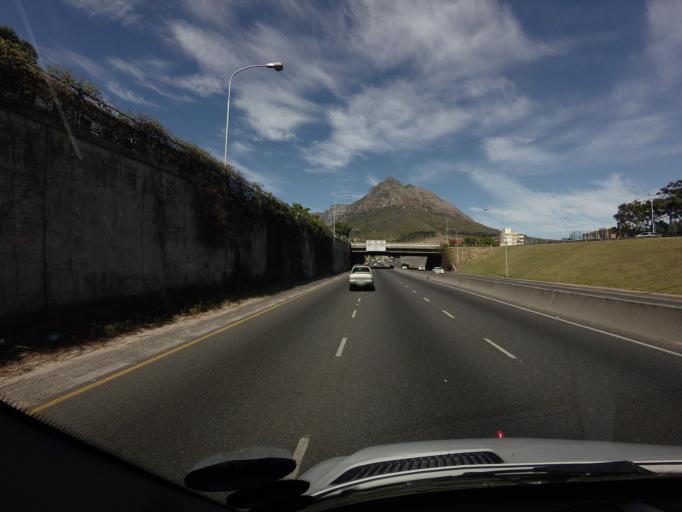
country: ZA
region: Western Cape
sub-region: City of Cape Town
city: Rosebank
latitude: -33.9451
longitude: 18.4714
